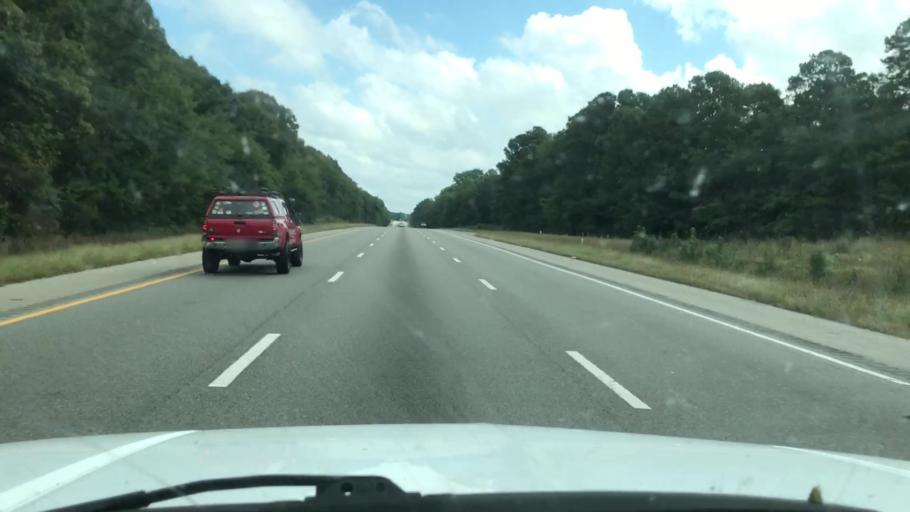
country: US
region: Virginia
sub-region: Henrico County
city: Short Pump
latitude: 37.6720
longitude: -77.5758
